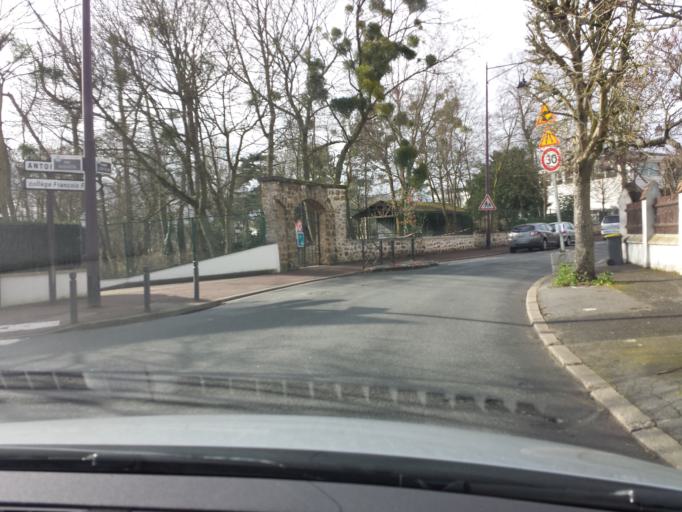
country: FR
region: Ile-de-France
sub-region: Departement des Hauts-de-Seine
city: Antony
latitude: 48.7567
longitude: 2.2992
